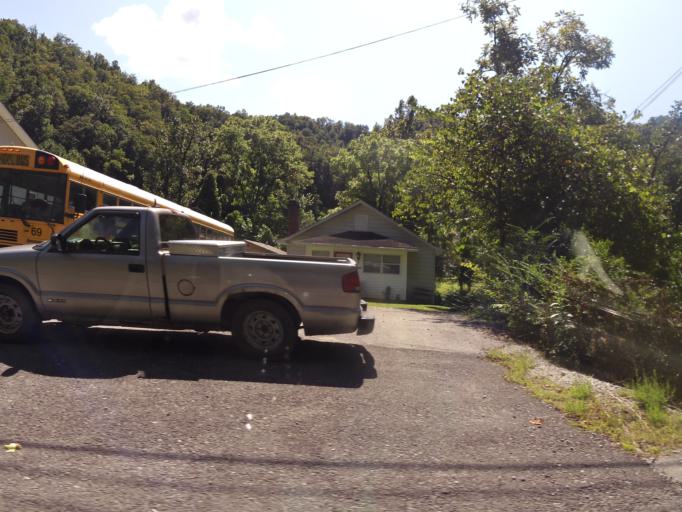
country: US
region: Kentucky
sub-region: Leslie County
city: Hyden
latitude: 37.1525
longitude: -83.3894
